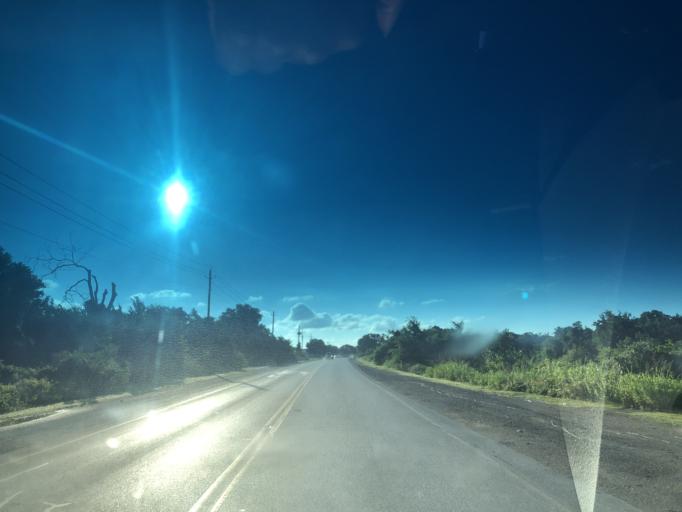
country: US
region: Texas
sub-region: Dallas County
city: Grand Prairie
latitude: 32.7778
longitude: -97.0134
